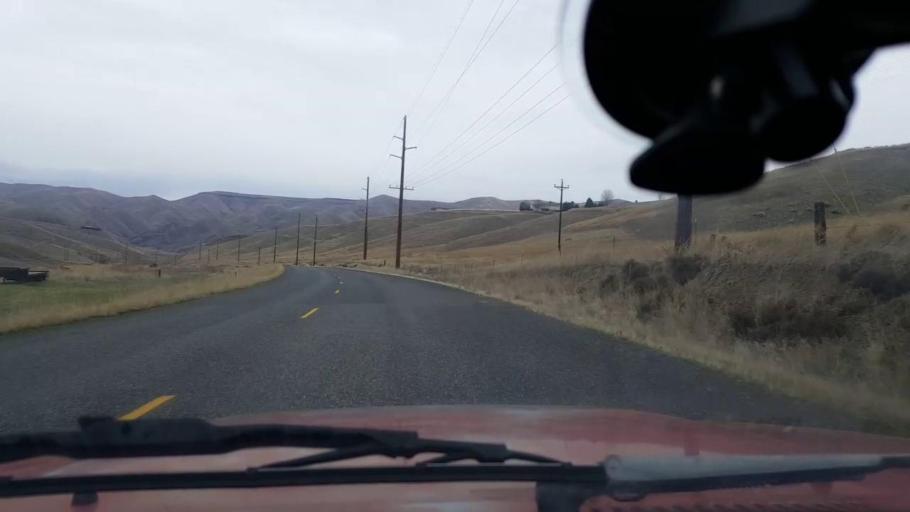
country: US
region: Washington
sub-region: Asotin County
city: Clarkston Heights-Vineland
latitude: 46.4025
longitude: -117.1017
